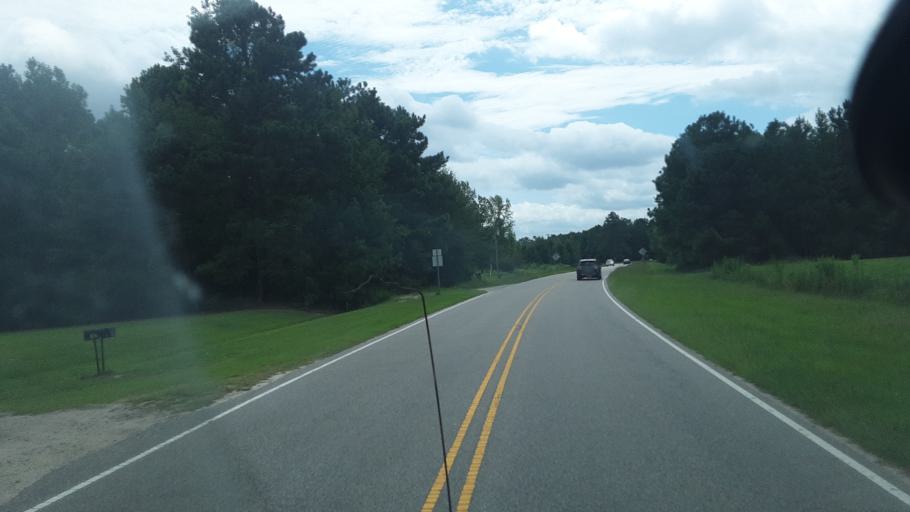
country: US
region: North Carolina
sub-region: Robeson County
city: Fairmont
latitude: 34.3988
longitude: -79.1248
